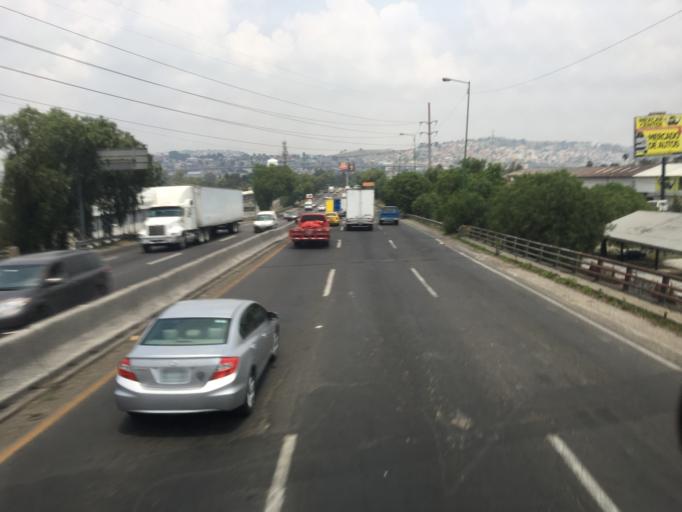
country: MX
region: Mexico
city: Tlalnepantla
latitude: 19.5603
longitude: -99.1946
